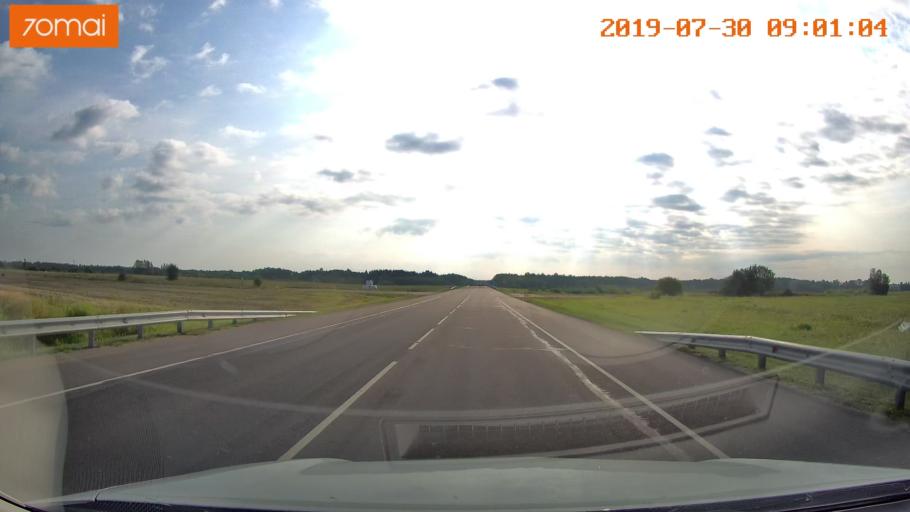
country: RU
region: Kaliningrad
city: Gusev
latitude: 54.6157
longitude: 22.1982
